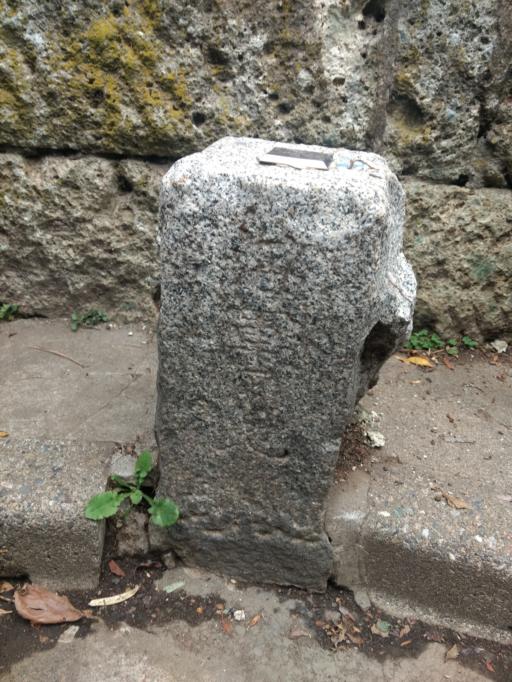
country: JP
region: Saitama
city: Kawaguchi
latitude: 35.7447
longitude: 139.7352
